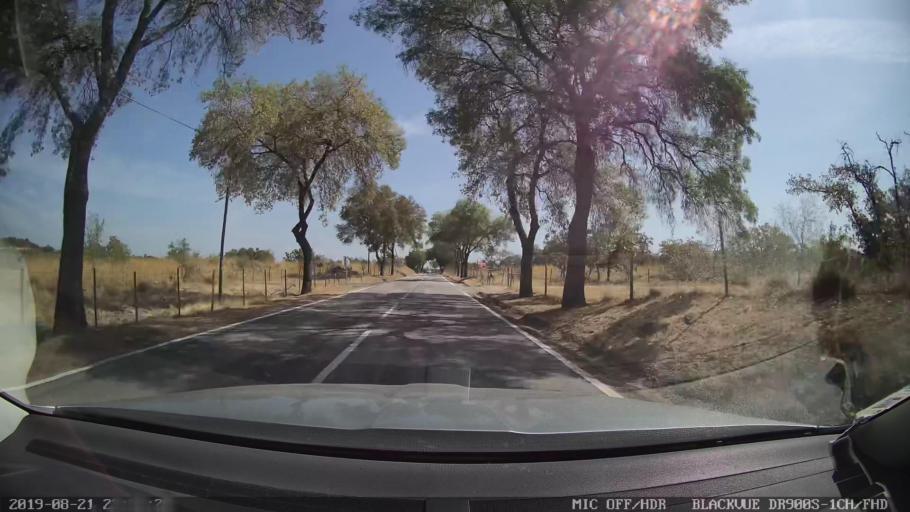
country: PT
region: Guarda
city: Alcains
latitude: 39.8736
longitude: -7.4291
